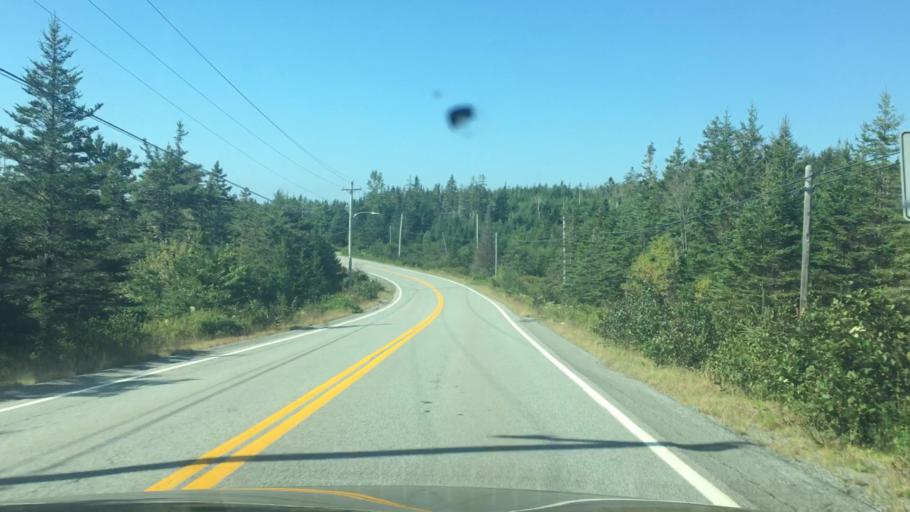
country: CA
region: Nova Scotia
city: New Glasgow
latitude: 44.8081
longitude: -62.6893
